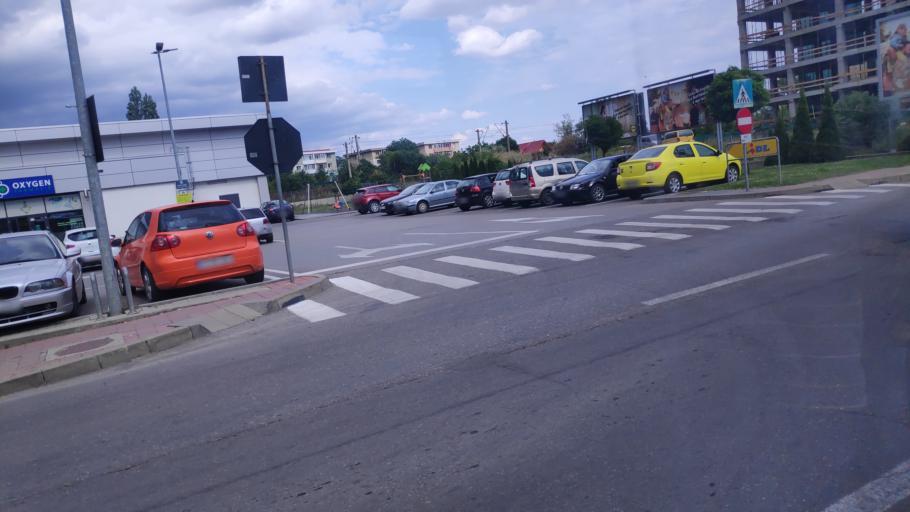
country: RO
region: Iasi
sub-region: Municipiul Iasi
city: Iasi
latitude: 47.1518
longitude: 27.5727
